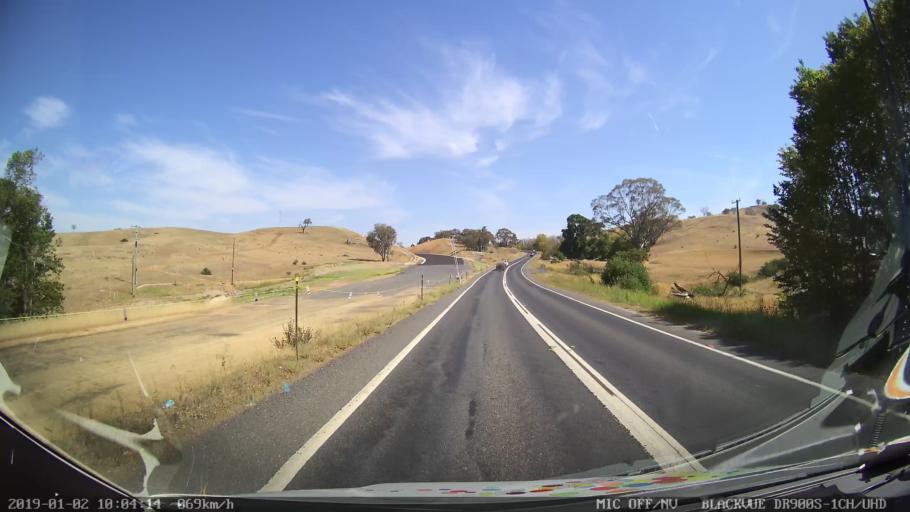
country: AU
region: New South Wales
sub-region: Gundagai
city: Gundagai
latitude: -35.1698
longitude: 148.1236
